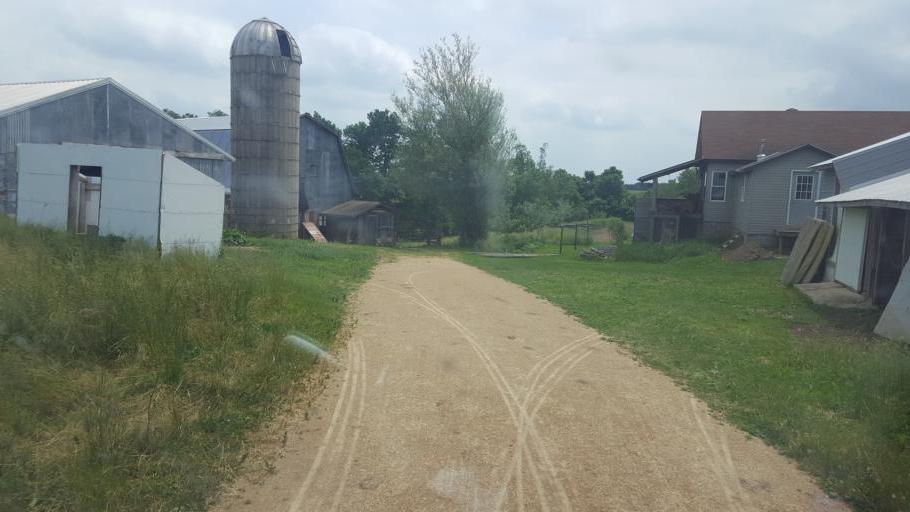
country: US
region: Wisconsin
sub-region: Vernon County
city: Hillsboro
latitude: 43.6058
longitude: -90.4314
